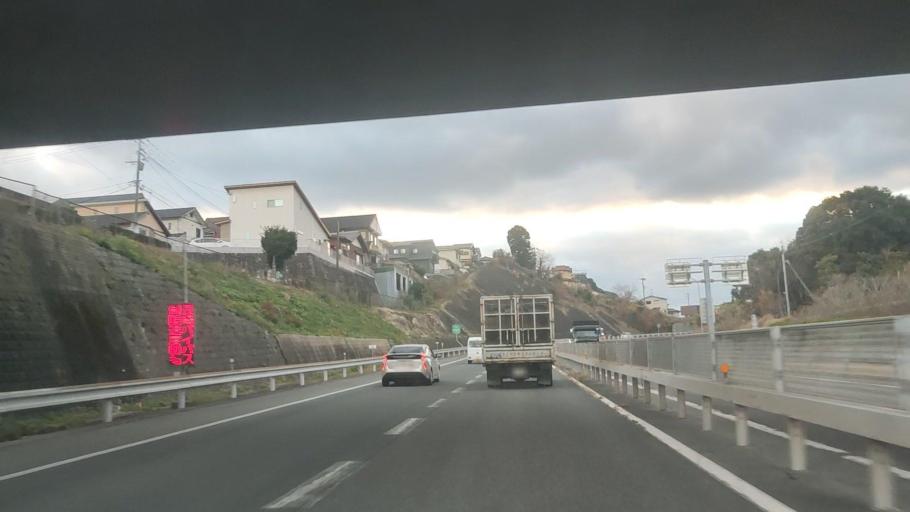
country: JP
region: Nagasaki
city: Obita
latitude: 32.8133
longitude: 129.9627
